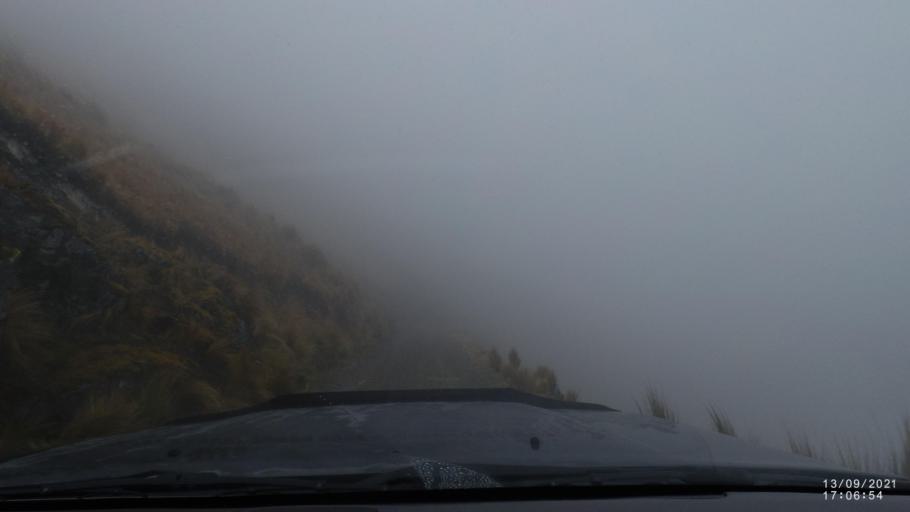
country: BO
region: Cochabamba
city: Colomi
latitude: -17.3276
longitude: -65.7227
